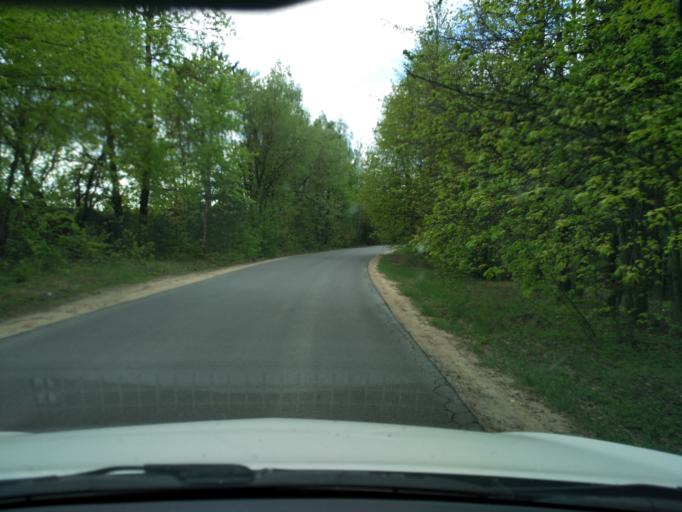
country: LT
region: Vilnius County
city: Rasos
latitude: 54.6941
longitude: 25.3323
